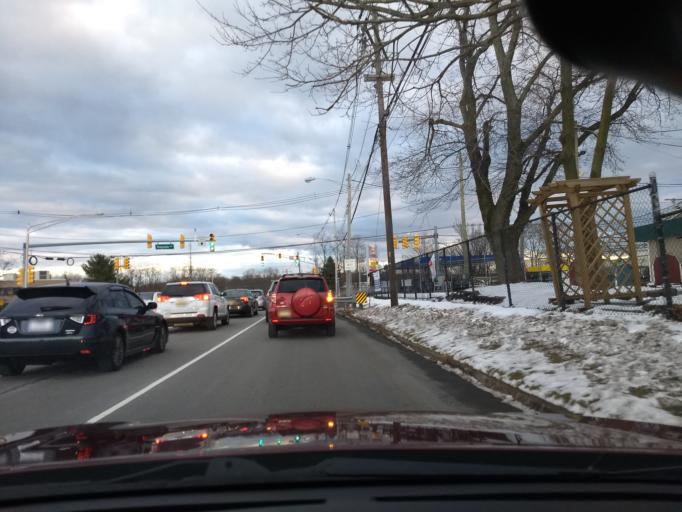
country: US
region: New Jersey
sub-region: Morris County
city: Morristown
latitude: 40.8075
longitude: -74.4628
